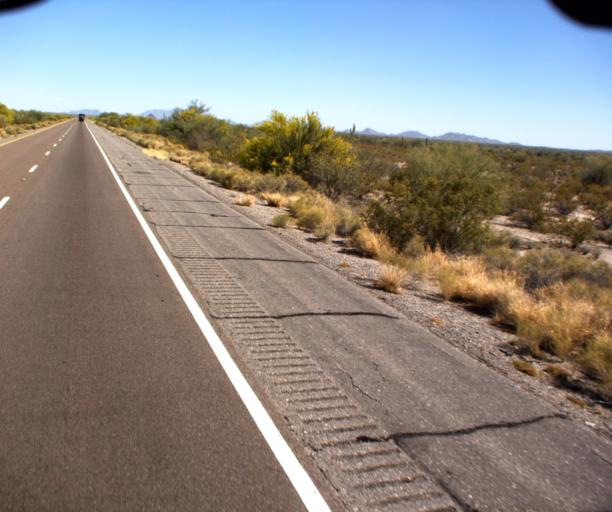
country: US
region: Arizona
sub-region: Maricopa County
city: Gila Bend
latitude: 32.8564
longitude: -112.3802
